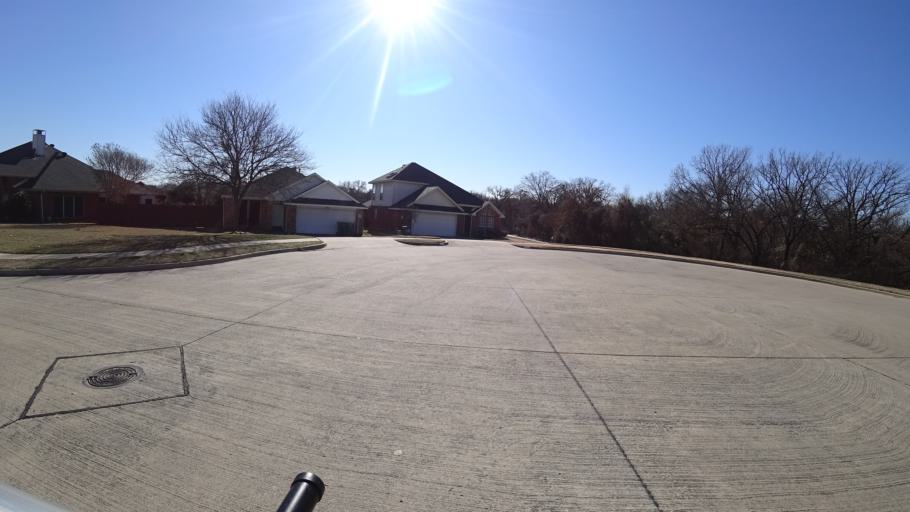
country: US
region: Texas
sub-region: Denton County
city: Lewisville
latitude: 33.0229
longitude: -97.0251
